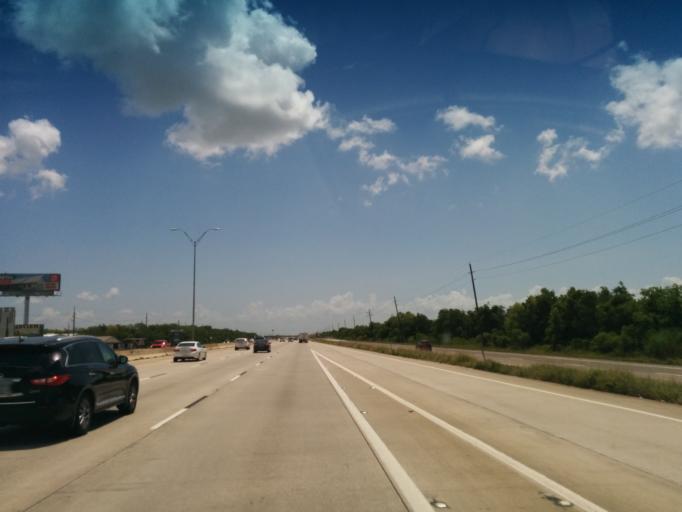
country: US
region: Texas
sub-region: Chambers County
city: Mont Belvieu
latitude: 29.8248
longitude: -94.8599
